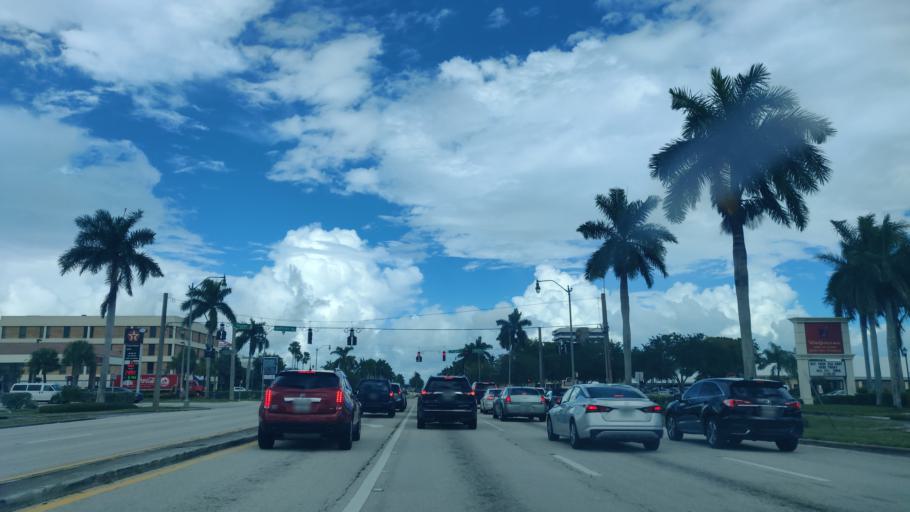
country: US
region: Florida
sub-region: Palm Beach County
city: Schall Circle
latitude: 26.7111
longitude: -80.0965
